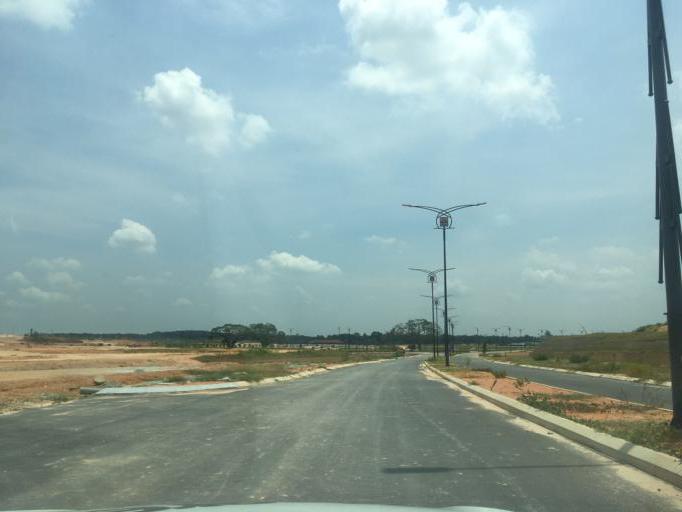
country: MY
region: Putrajaya
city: Putrajaya
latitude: 2.8449
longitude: 101.7090
